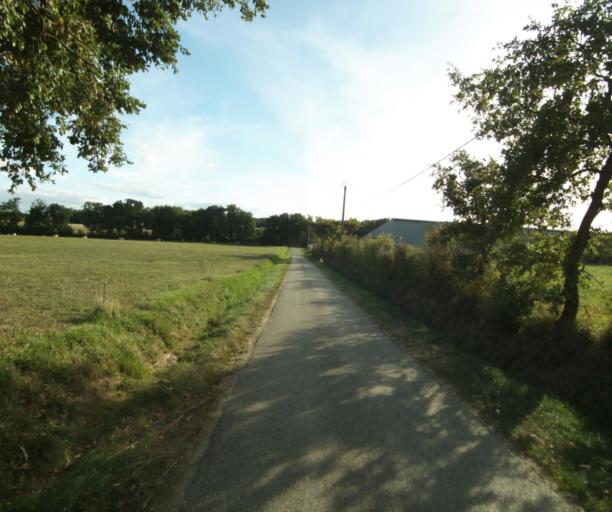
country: FR
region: Midi-Pyrenees
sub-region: Departement du Gers
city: Gondrin
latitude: 43.9106
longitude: 0.2456
